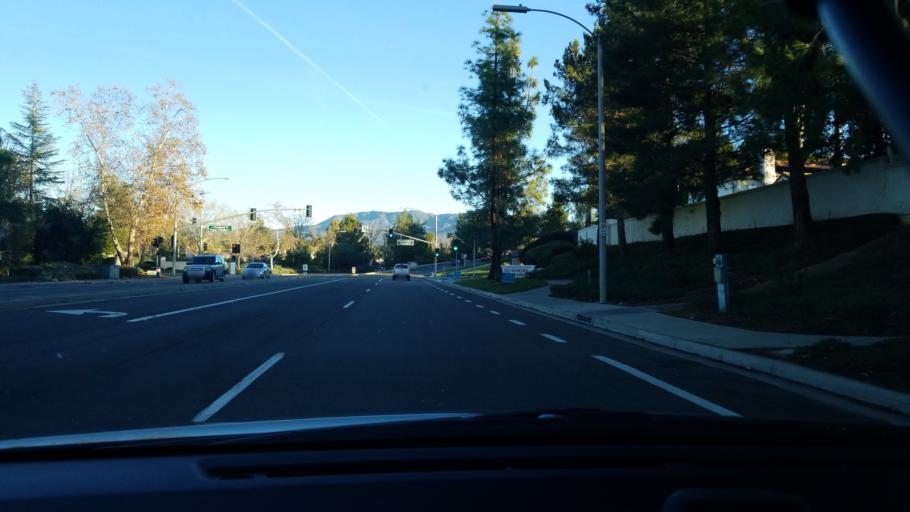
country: US
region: California
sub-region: Riverside County
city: Temecula
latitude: 33.4763
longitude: -117.0965
